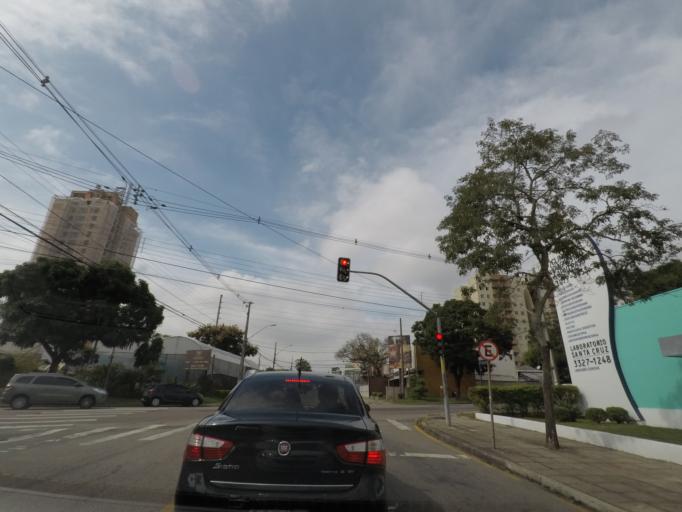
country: BR
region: Parana
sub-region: Curitiba
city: Curitiba
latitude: -25.4890
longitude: -49.2963
